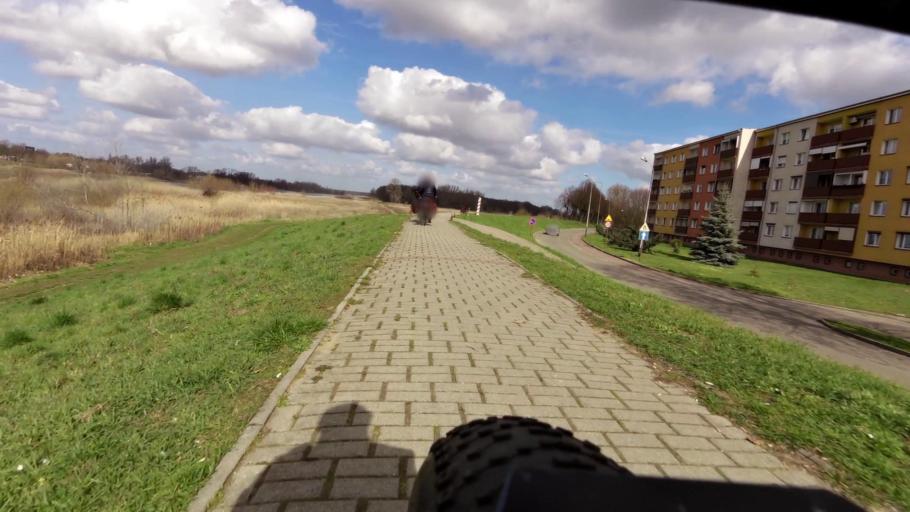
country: PL
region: Lubusz
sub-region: Powiat slubicki
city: Slubice
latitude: 52.3538
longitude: 14.5555
